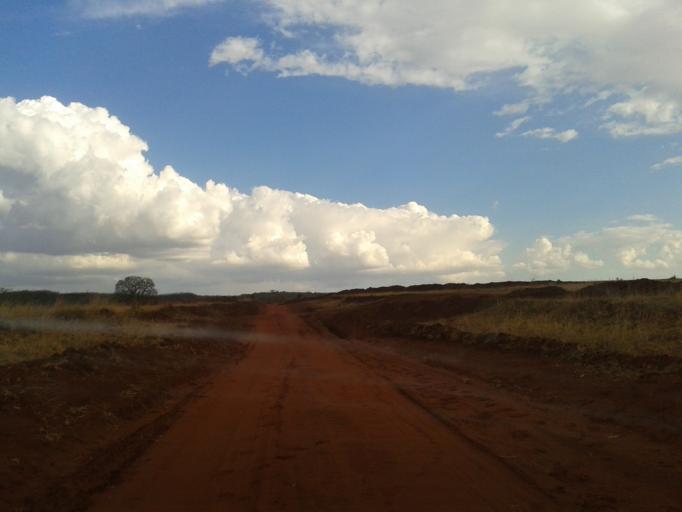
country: BR
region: Minas Gerais
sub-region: Santa Vitoria
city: Santa Vitoria
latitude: -19.1889
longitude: -49.9421
